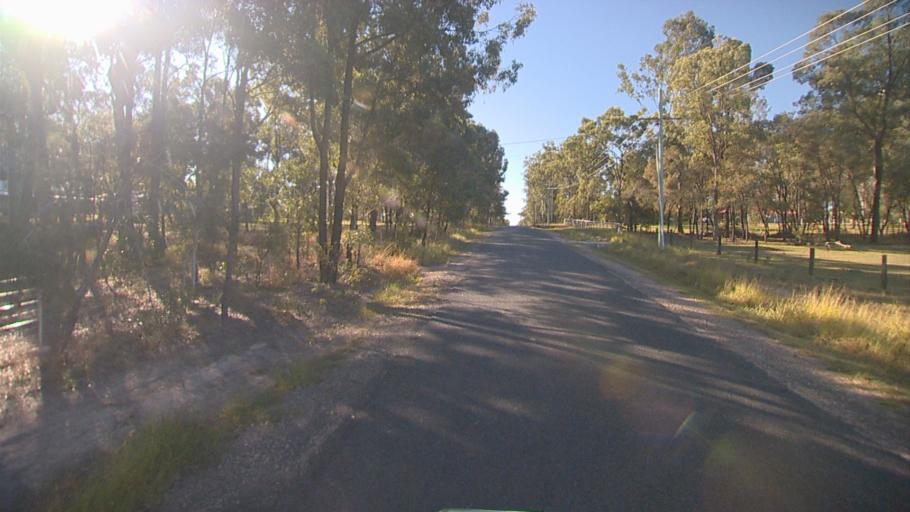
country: AU
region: Queensland
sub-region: Logan
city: Logan Reserve
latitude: -27.7191
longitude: 153.1065
